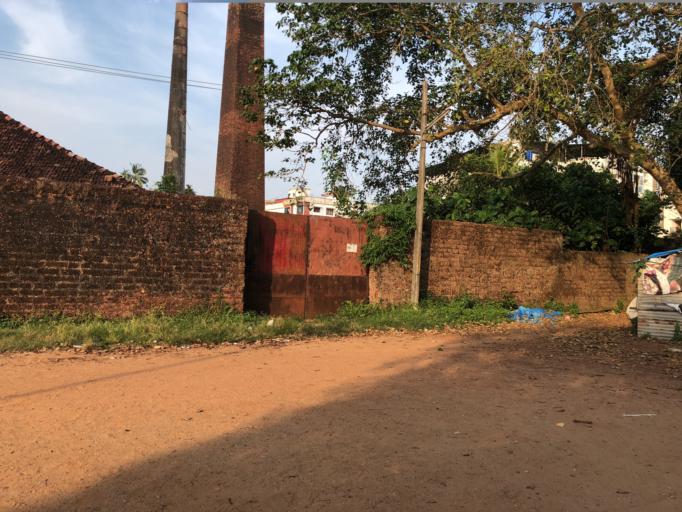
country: IN
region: Karnataka
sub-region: Dakshina Kannada
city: Ullal
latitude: 12.8433
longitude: 74.8424
